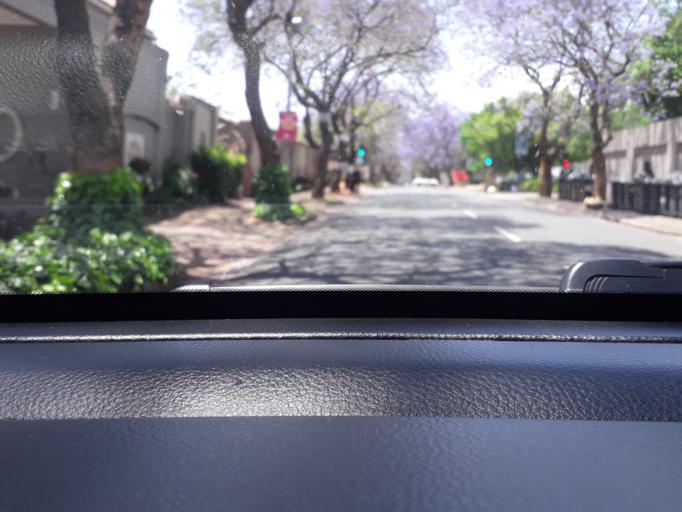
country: ZA
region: Gauteng
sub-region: City of Johannesburg Metropolitan Municipality
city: Johannesburg
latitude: -26.1466
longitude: 28.0622
